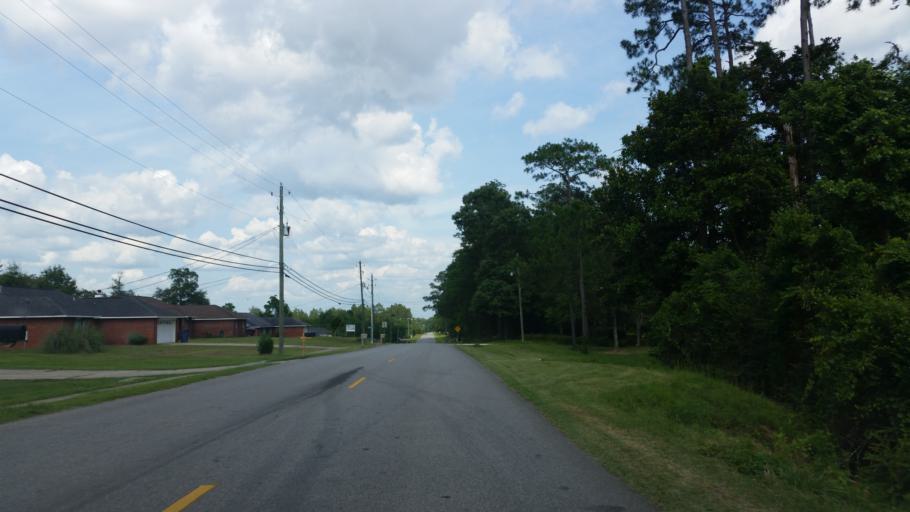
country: US
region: Florida
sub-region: Escambia County
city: Gonzalez
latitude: 30.5691
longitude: -87.2555
